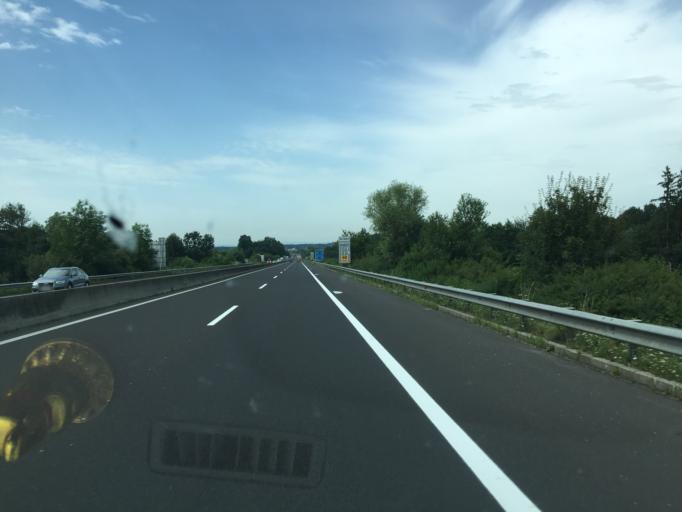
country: AT
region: Upper Austria
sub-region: Wels-Land
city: Sattledt
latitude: 48.0260
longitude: 14.0647
